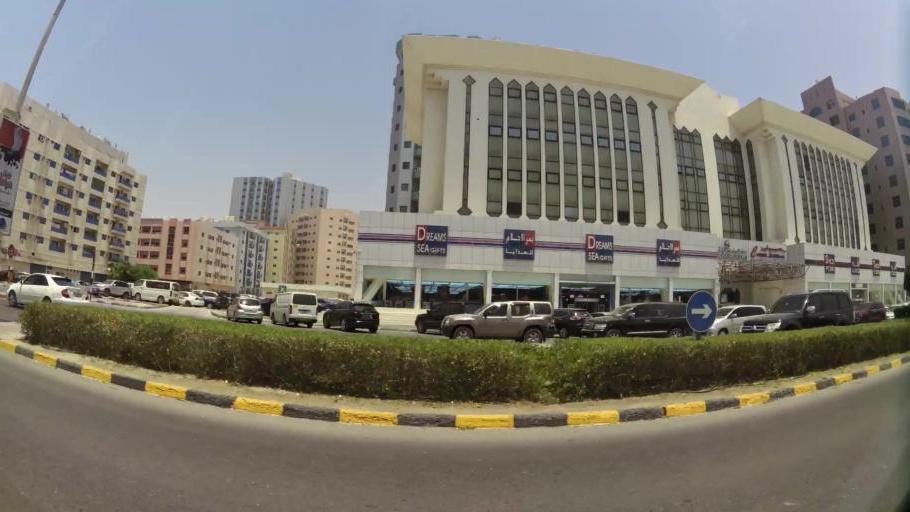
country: AE
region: Ajman
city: Ajman
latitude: 25.4093
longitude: 55.4435
